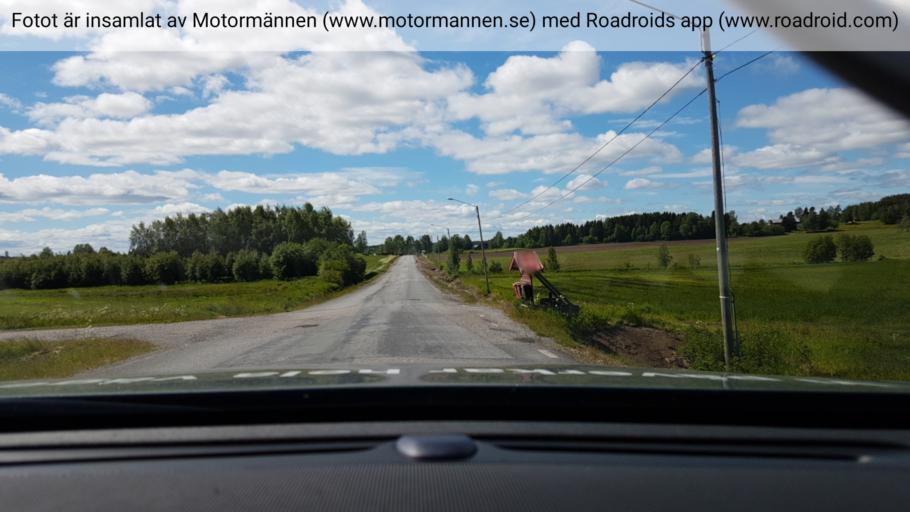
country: SE
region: Vaesterbotten
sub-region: Skelleftea Kommun
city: Burea
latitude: 64.3928
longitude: 21.3272
